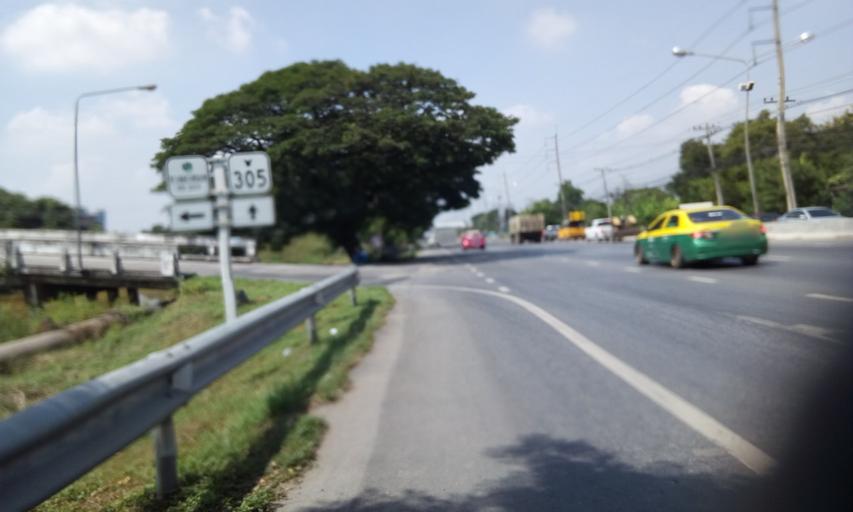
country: TH
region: Pathum Thani
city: Ban Rangsit
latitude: 14.0489
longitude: 100.8134
